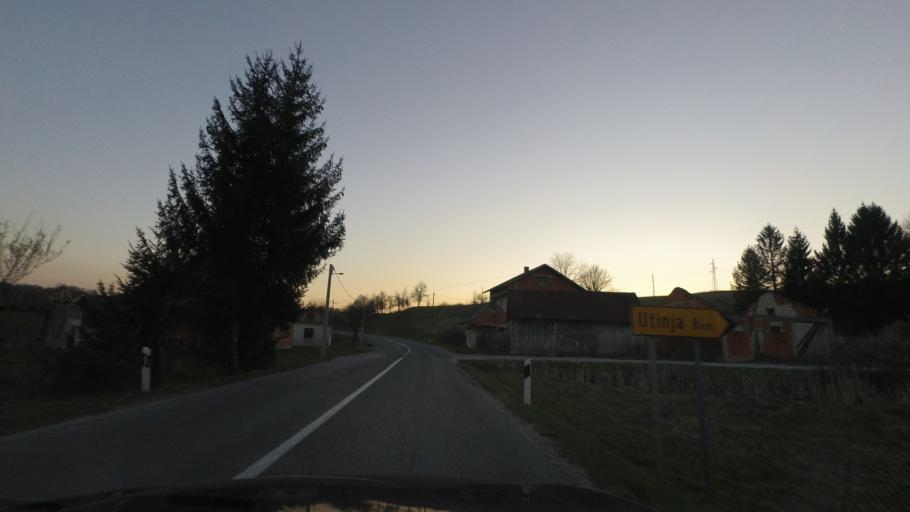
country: HR
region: Karlovacka
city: Vojnic
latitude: 45.3383
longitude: 15.7231
